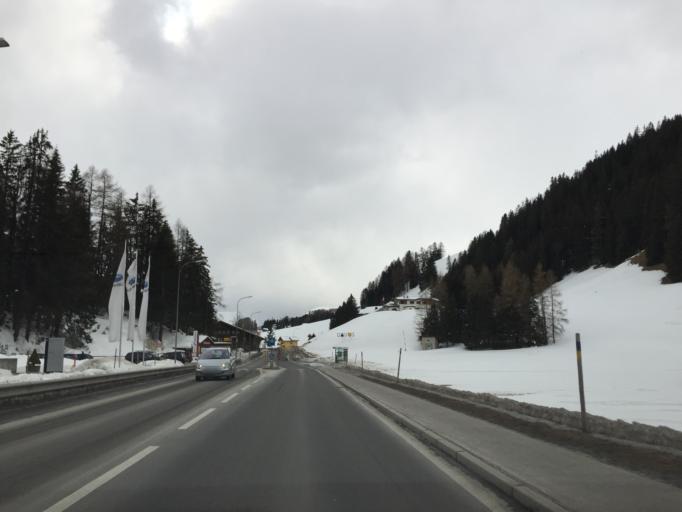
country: CH
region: Grisons
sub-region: Praettigau/Davos District
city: Davos
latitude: 46.8253
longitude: 9.8540
